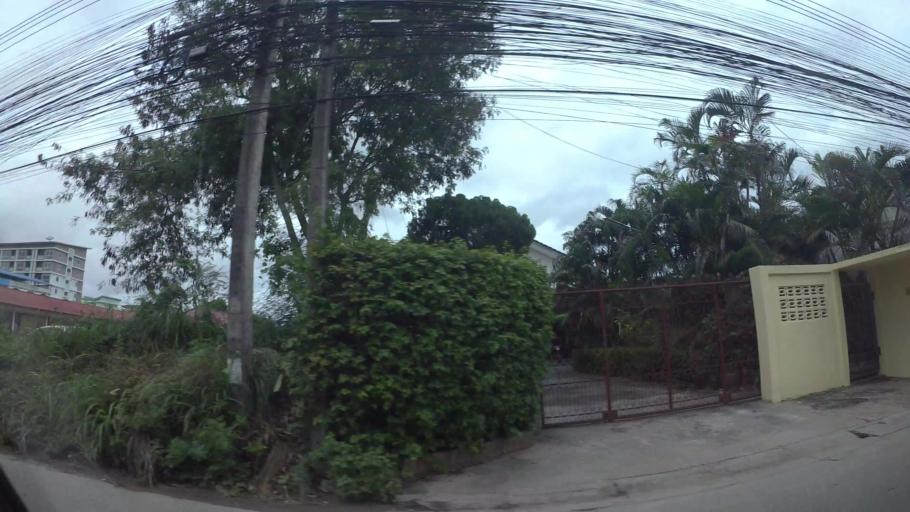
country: TH
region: Rayong
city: Rayong
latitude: 12.6796
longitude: 101.2552
